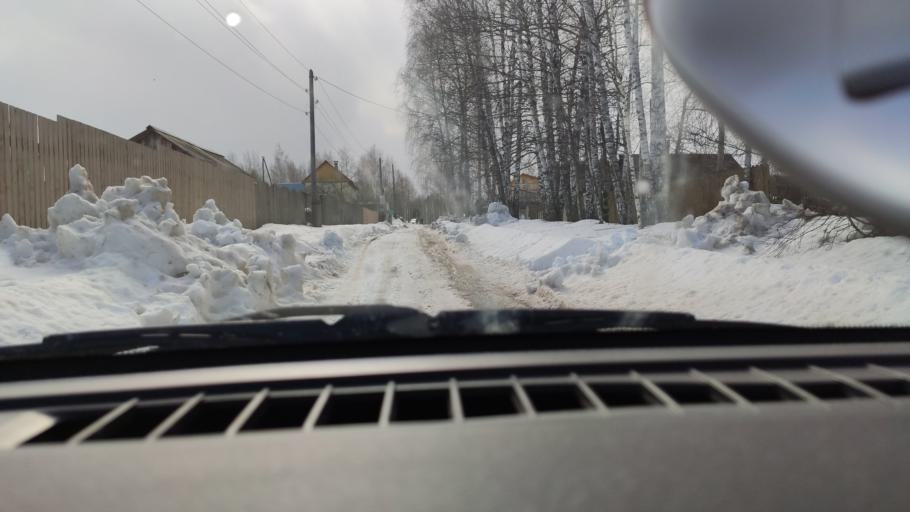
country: RU
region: Perm
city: Nytva
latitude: 57.9246
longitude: 55.4348
